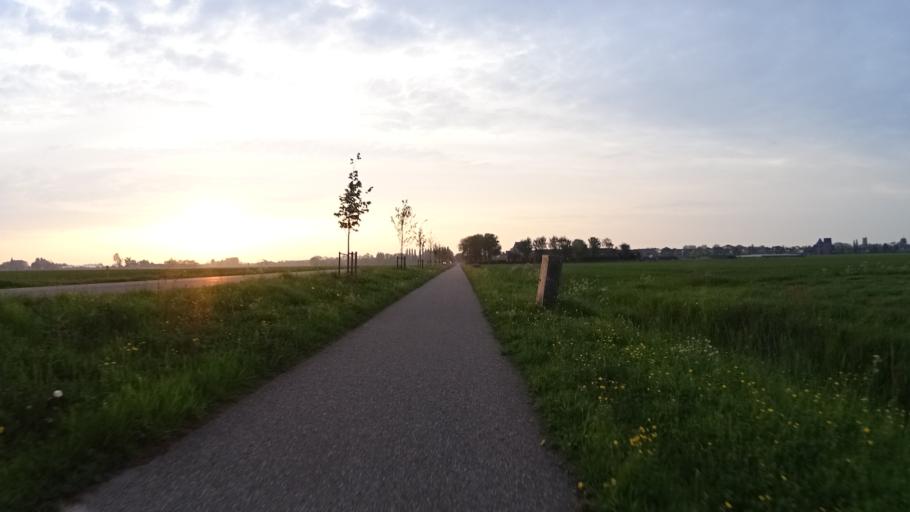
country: NL
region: North Brabant
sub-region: Gemeente Woudrichem
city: Woudrichem
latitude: 51.8031
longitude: 5.0053
